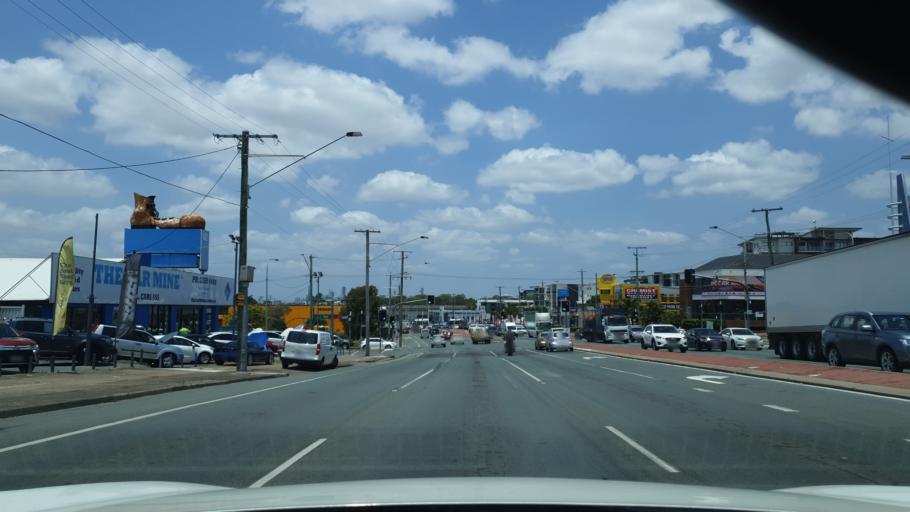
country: AU
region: Queensland
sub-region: Brisbane
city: Wavell Heights
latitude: -27.3927
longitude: 153.0312
